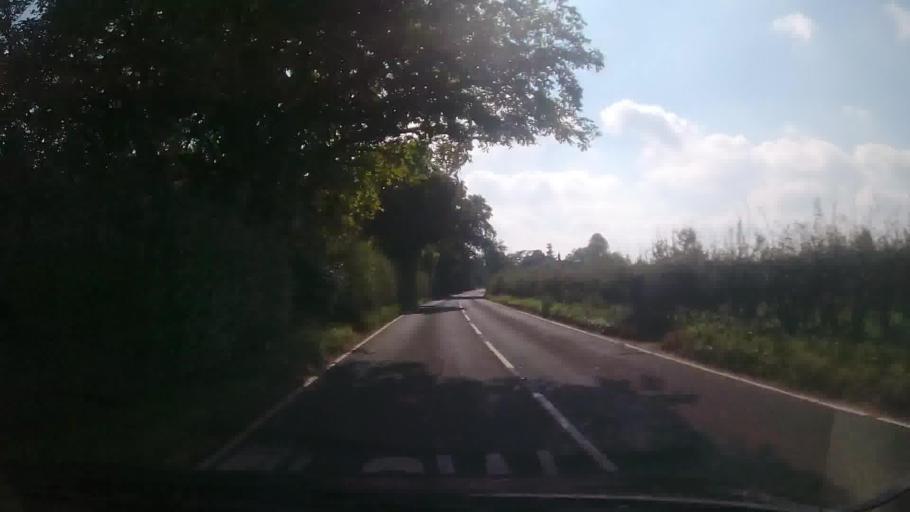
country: GB
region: England
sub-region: Cheshire West and Chester
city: Beeston
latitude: 53.1104
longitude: -2.6608
